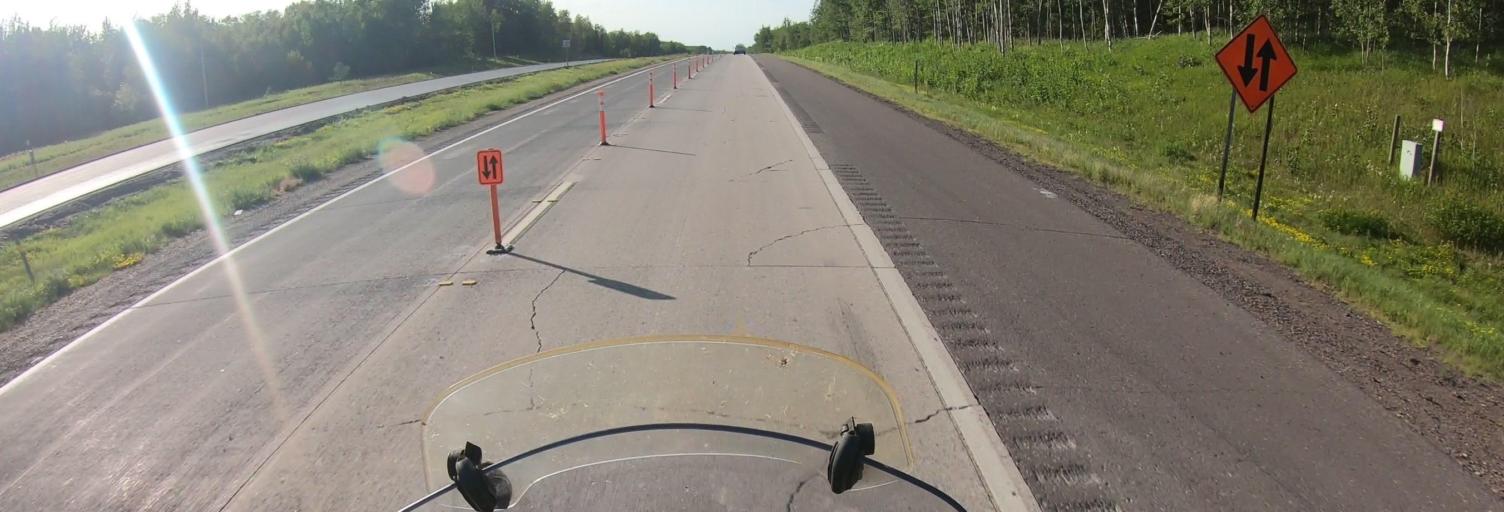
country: US
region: Minnesota
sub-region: Saint Louis County
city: Hermantown
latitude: 46.9013
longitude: -92.3752
